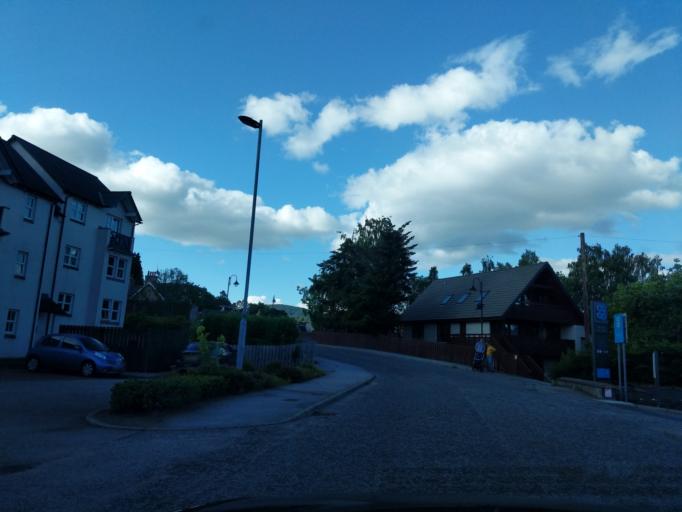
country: GB
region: Scotland
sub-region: Aberdeenshire
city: Aboyne
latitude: 57.0753
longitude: -2.7784
